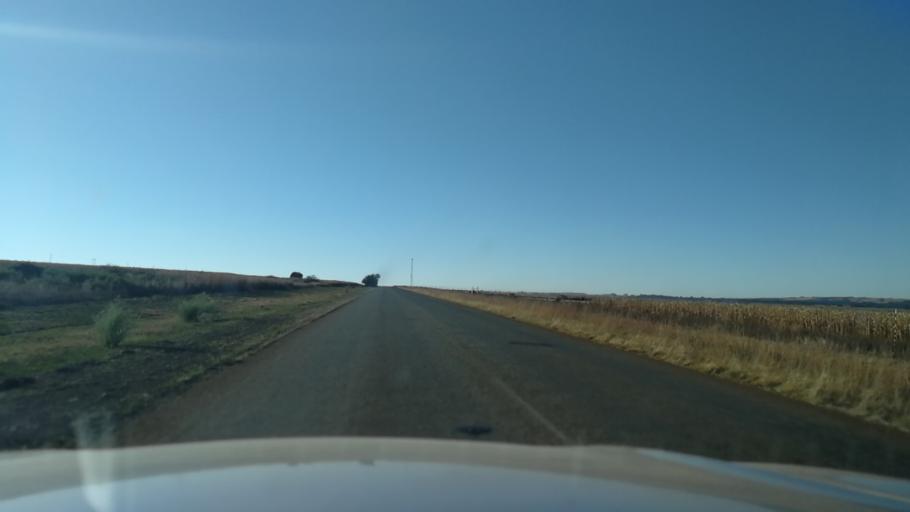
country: ZA
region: North-West
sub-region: Bojanala Platinum District Municipality
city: Rustenburg
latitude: -25.9970
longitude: 27.2999
